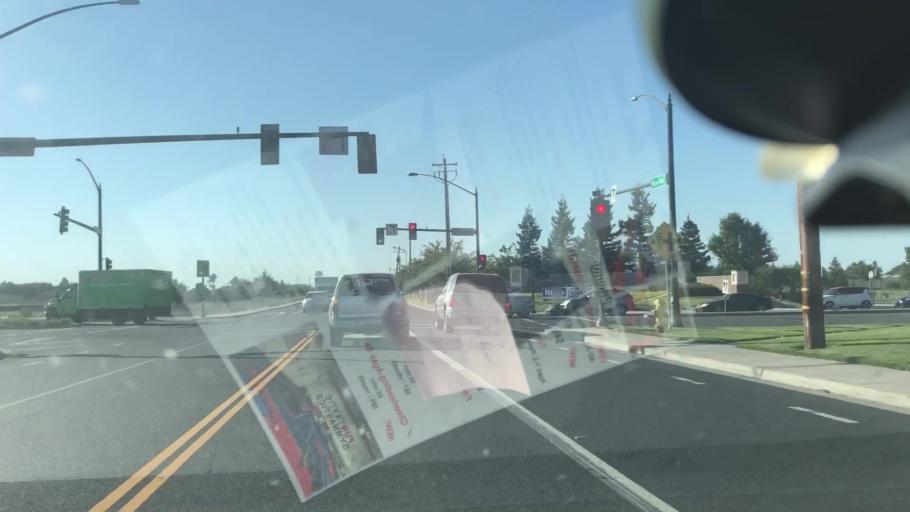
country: US
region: California
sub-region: San Joaquin County
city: Manteca
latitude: 37.7858
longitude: -121.1999
